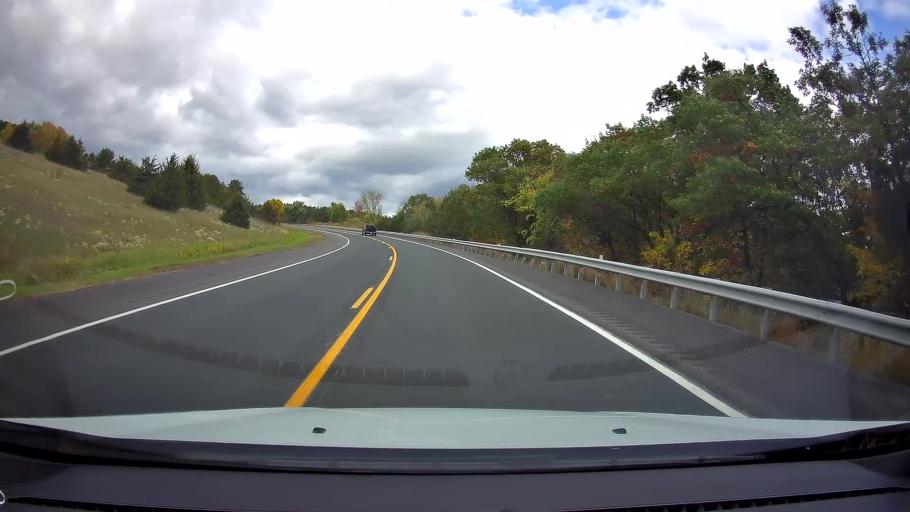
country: US
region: Wisconsin
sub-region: Polk County
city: Saint Croix Falls
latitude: 45.4155
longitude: -92.6533
